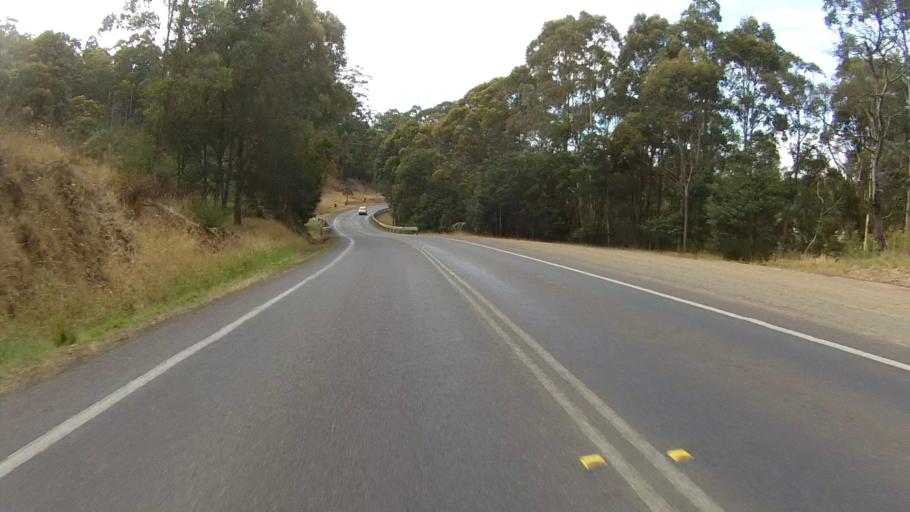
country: AU
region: Tasmania
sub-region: Kingborough
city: Kettering
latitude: -43.1003
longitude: 147.2434
